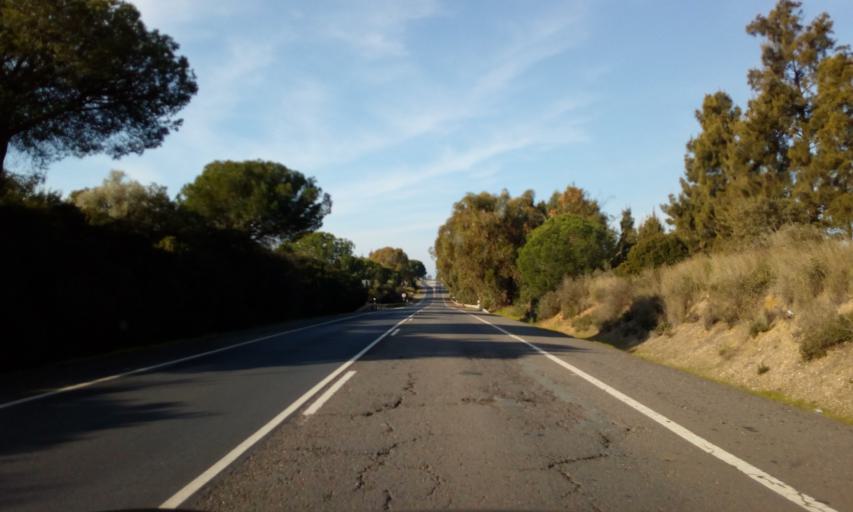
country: ES
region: Andalusia
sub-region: Provincia de Huelva
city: Isla Cristina
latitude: 37.2467
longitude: -7.2993
